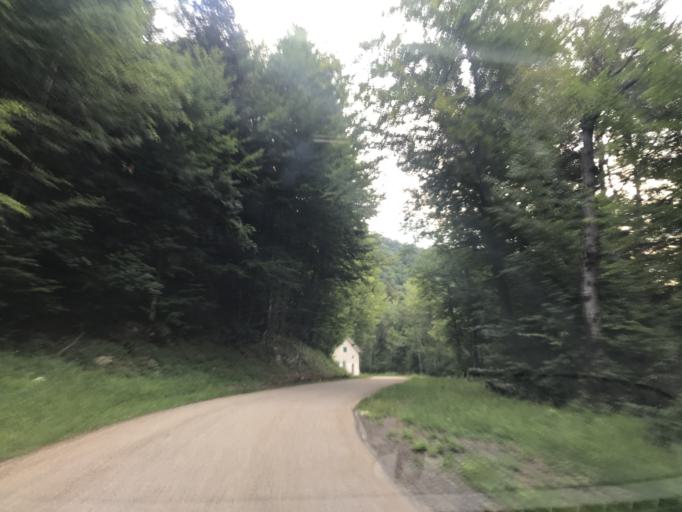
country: FR
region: Rhone-Alpes
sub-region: Departement de l'Isere
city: Saint-Vincent-de-Mercuze
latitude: 45.3779
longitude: 5.9207
